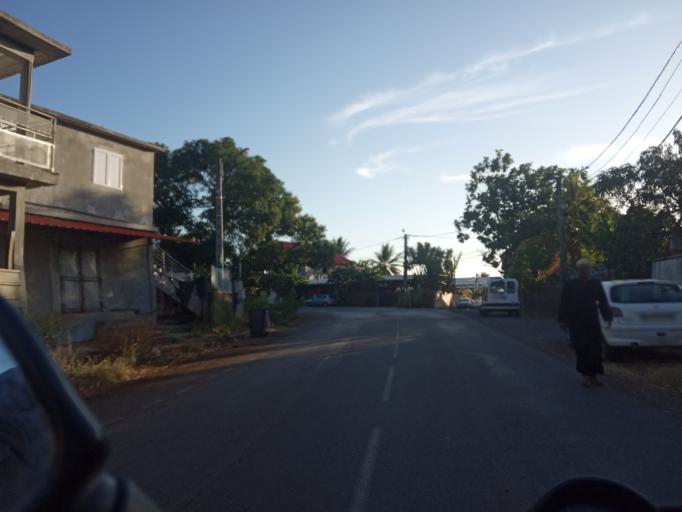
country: YT
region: Kani-Keli
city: Kani Keli
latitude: -12.9275
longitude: 45.1043
